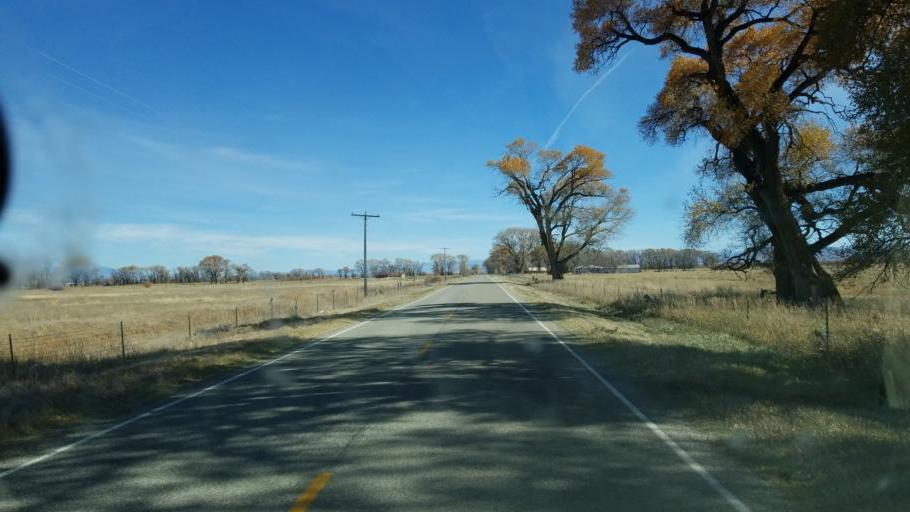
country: US
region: Colorado
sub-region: Conejos County
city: Conejos
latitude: 37.2835
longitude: -106.0510
